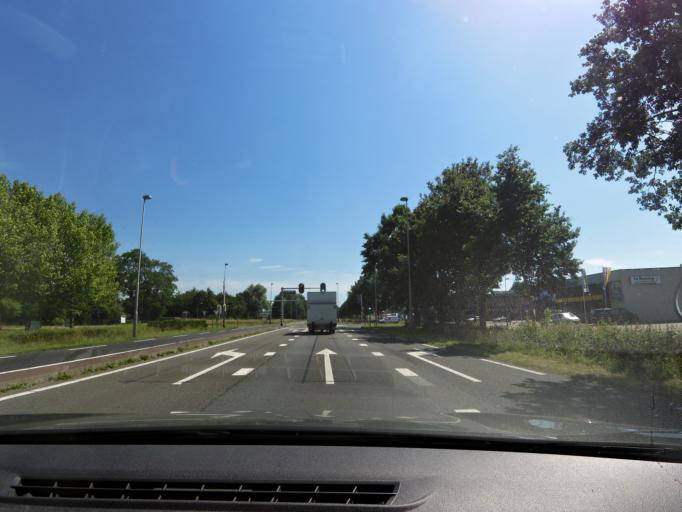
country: NL
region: Gelderland
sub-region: Berkelland
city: Eibergen
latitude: 52.0436
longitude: 6.6260
